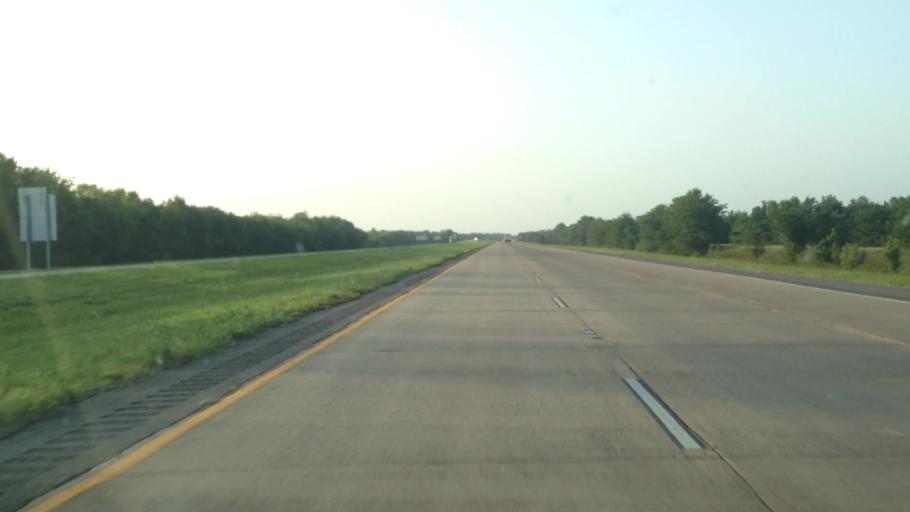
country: US
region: Louisiana
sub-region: Natchitoches Parish
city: Vienna Bend
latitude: 31.6040
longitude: -93.0449
